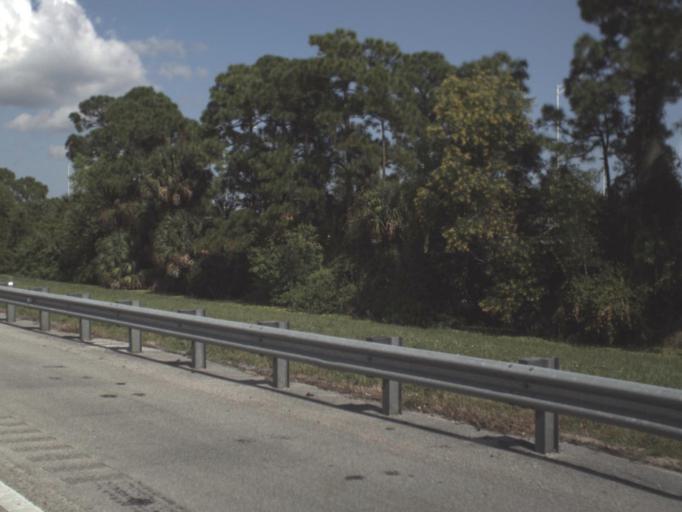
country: US
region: Florida
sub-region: Palm Beach County
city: Limestone Creek
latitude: 26.9026
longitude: -80.1396
